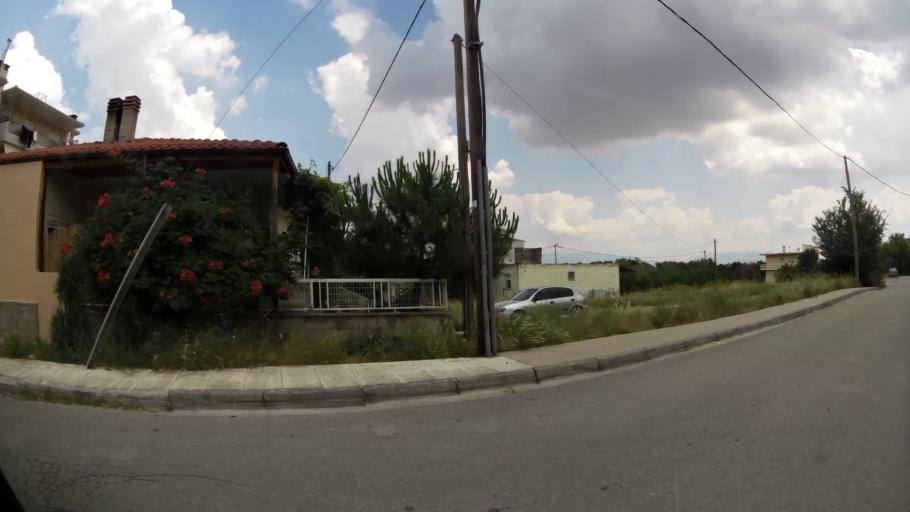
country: GR
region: West Macedonia
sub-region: Nomos Kozanis
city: Kozani
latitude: 40.2992
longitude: 21.8020
